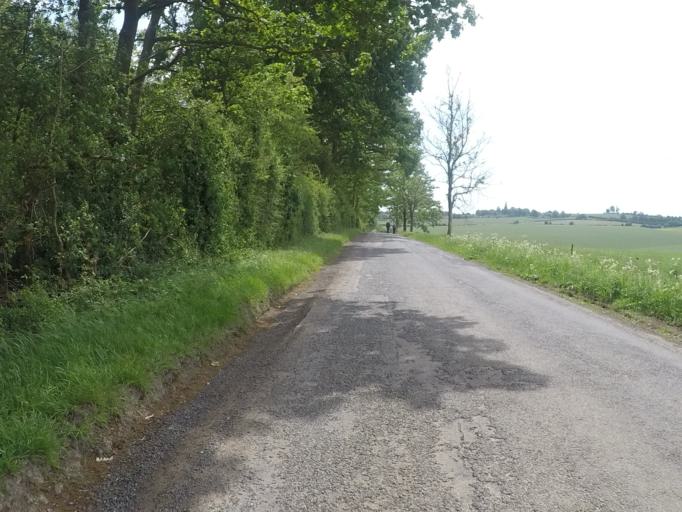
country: GB
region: England
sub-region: Oxfordshire
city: Charlbury
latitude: 51.8493
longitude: -1.5325
